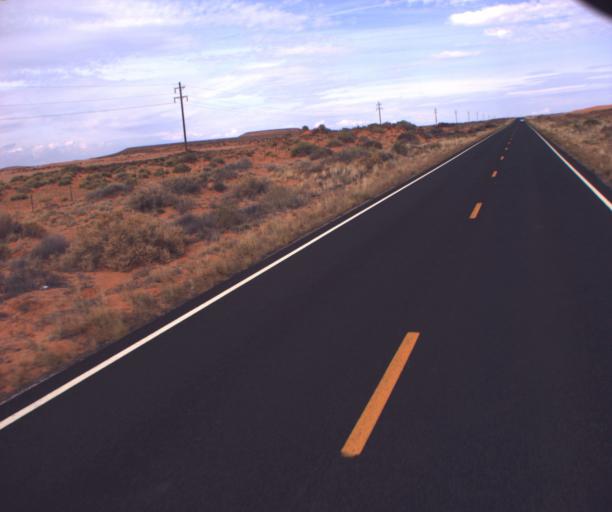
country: US
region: Arizona
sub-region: Apache County
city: Many Farms
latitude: 36.8183
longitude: -109.6457
